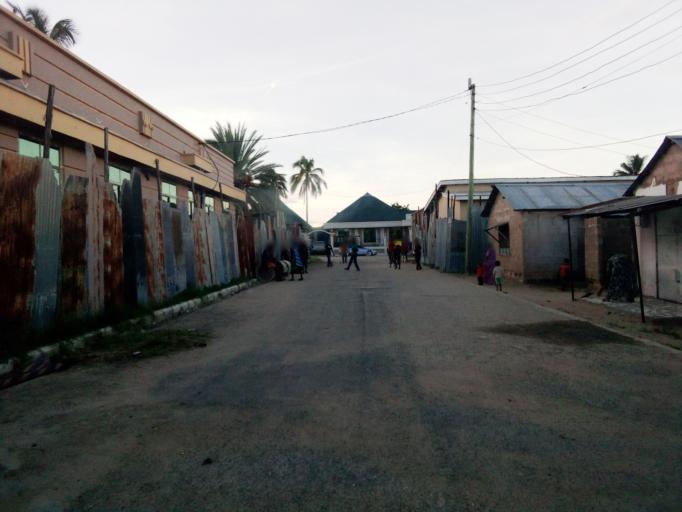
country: TZ
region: Dodoma
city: Dodoma
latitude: -6.1725
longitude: 35.7524
